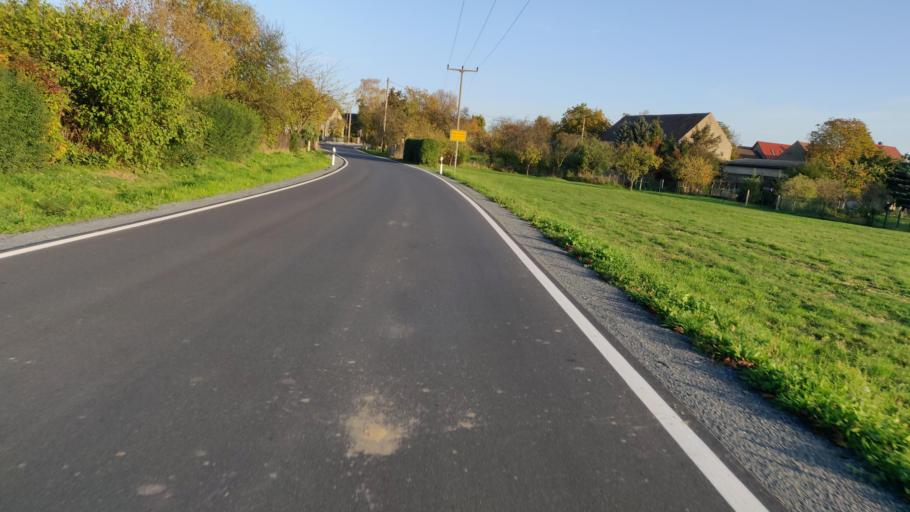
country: DE
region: Saxony
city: Lampertswalde
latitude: 51.3483
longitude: 13.6533
